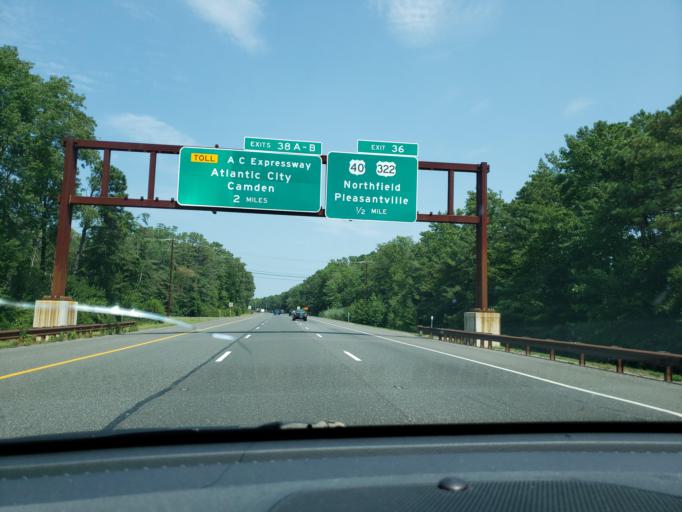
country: US
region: New Jersey
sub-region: Atlantic County
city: Northfield
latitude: 39.3865
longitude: -74.5719
